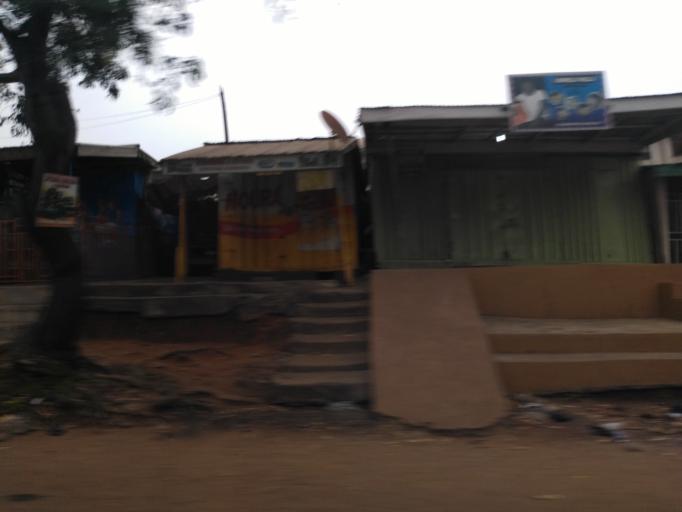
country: GH
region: Ashanti
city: Tafo
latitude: 6.7131
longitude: -1.6194
